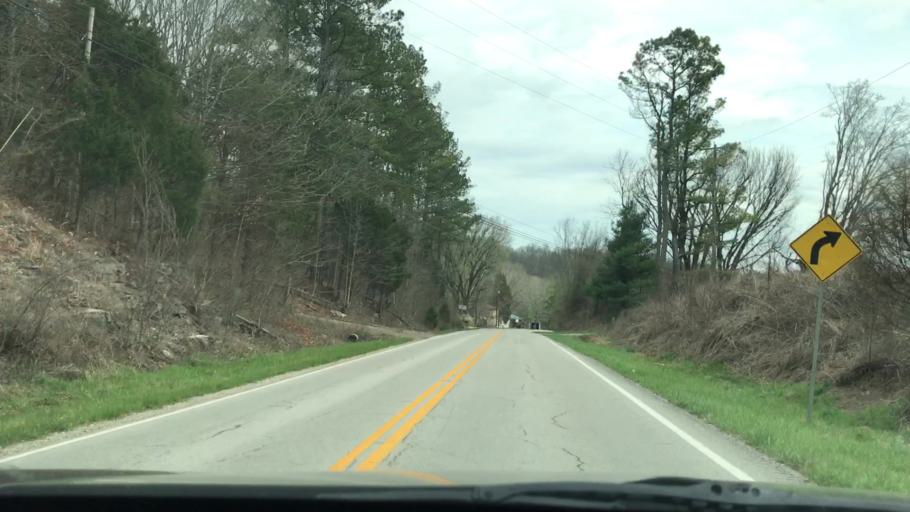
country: US
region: Kentucky
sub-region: Hart County
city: Munfordville
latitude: 37.3286
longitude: -85.7646
